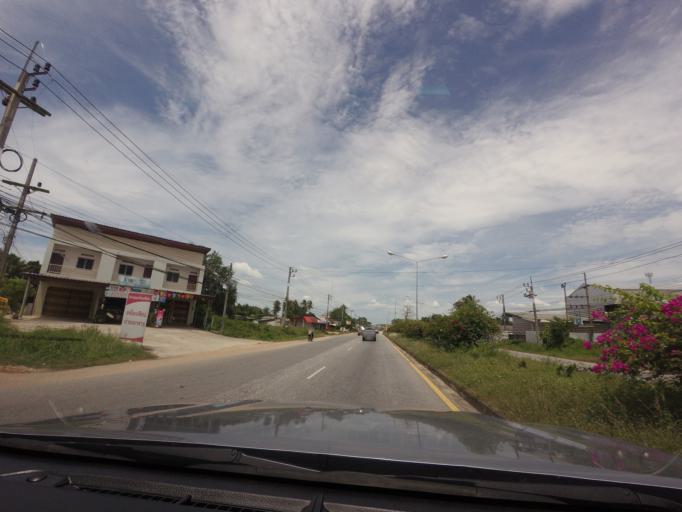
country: TH
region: Songkhla
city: Singhanakhon
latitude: 7.2434
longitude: 100.5436
